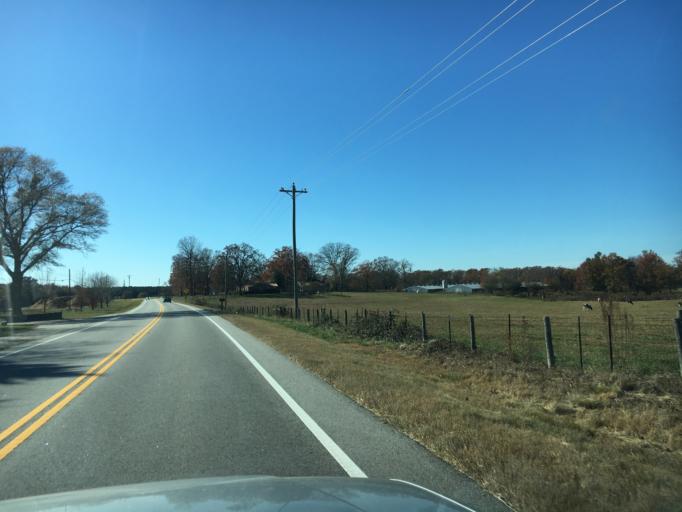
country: US
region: Georgia
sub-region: Hart County
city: Hartwell
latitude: 34.3166
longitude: -82.9912
